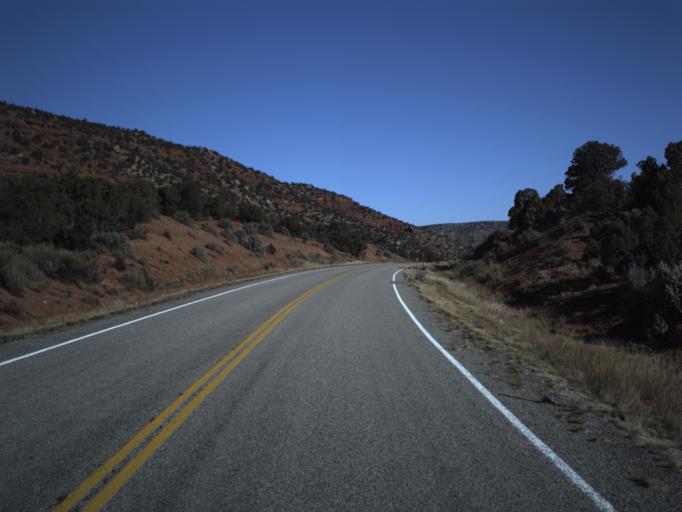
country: US
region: Utah
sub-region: San Juan County
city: Blanding
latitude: 37.5714
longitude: -110.0370
